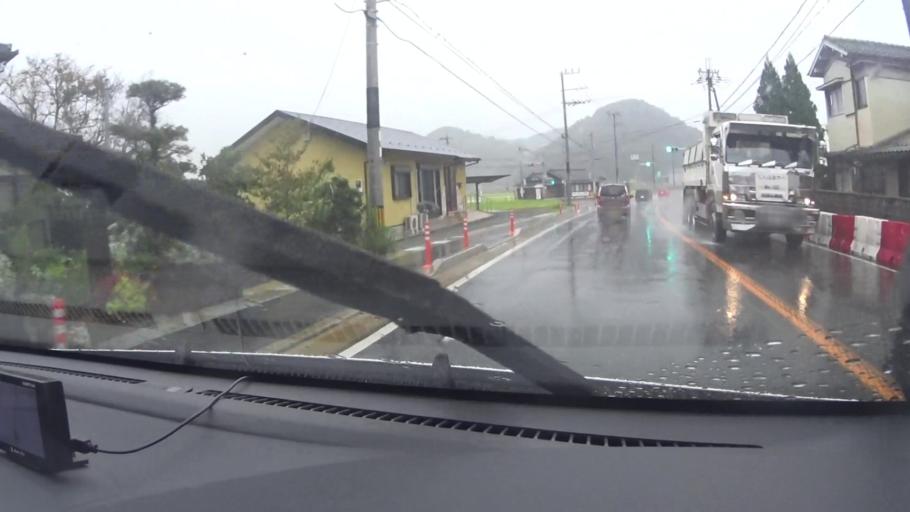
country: JP
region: Kyoto
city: Ayabe
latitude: 35.1769
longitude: 135.4038
